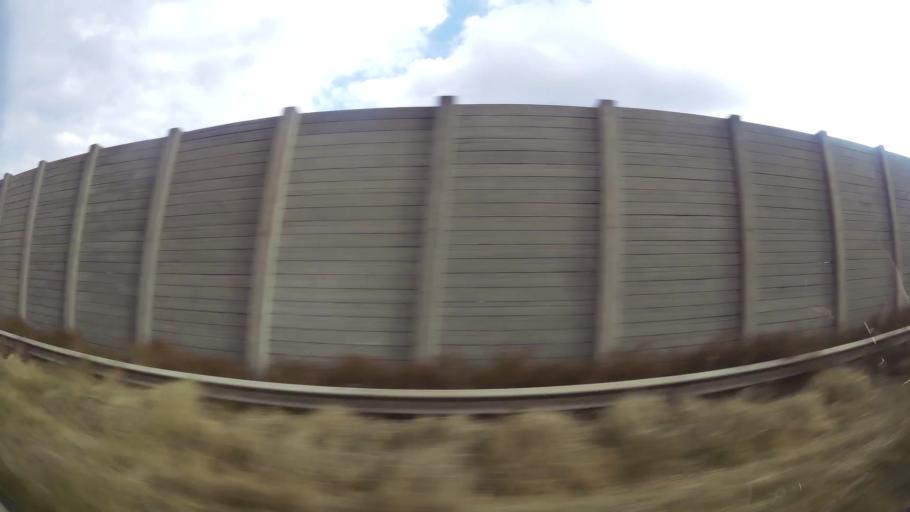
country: ZA
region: Orange Free State
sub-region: Fezile Dabi District Municipality
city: Sasolburg
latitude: -26.8283
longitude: 27.8518
